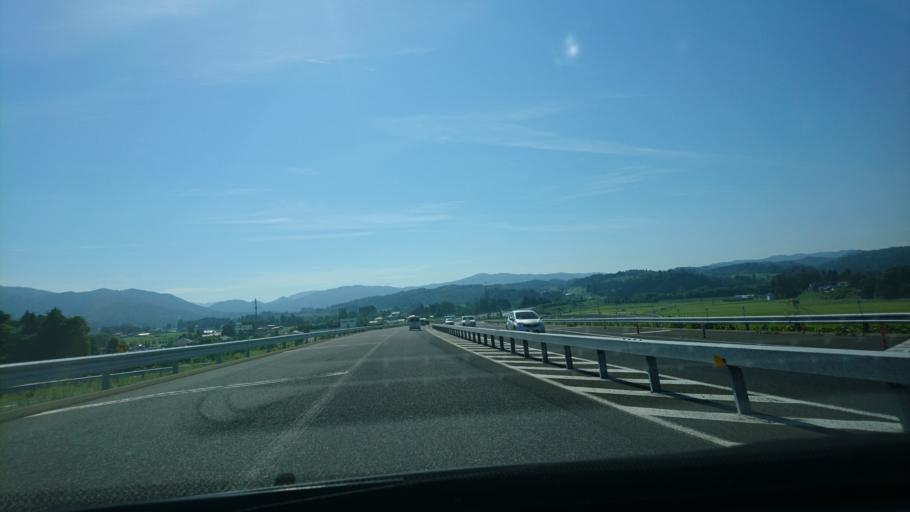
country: JP
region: Iwate
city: Hanamaki
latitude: 39.3839
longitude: 141.2167
